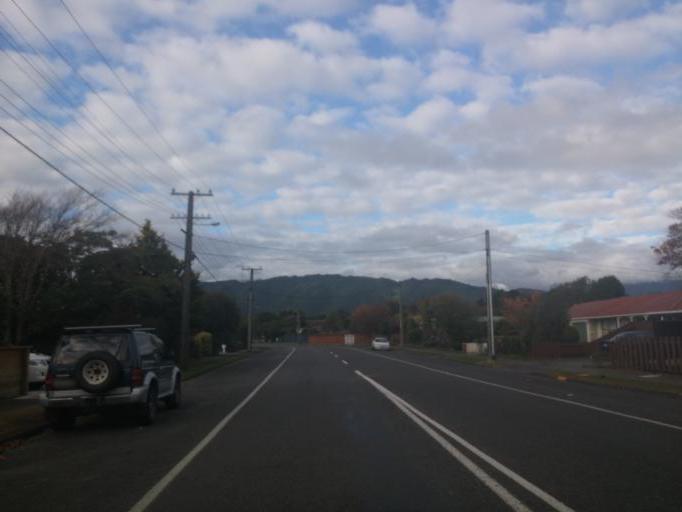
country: NZ
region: Wellington
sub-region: Kapiti Coast District
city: Paraparaumu
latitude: -40.8721
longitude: 175.0368
